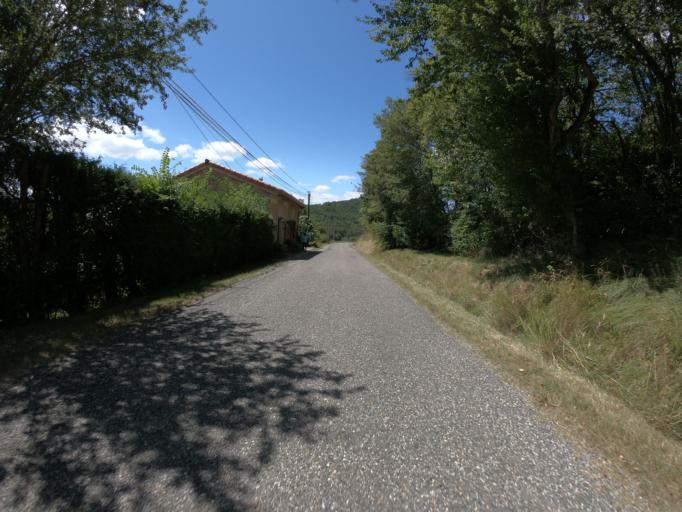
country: FR
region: Midi-Pyrenees
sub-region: Departement de l'Ariege
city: Mirepoix
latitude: 43.0485
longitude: 1.8236
